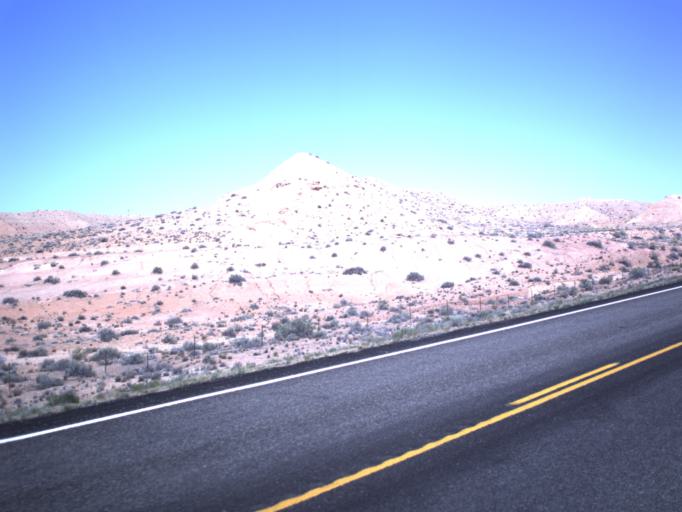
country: US
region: Utah
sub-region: Emery County
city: Ferron
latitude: 38.4057
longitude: -110.6928
